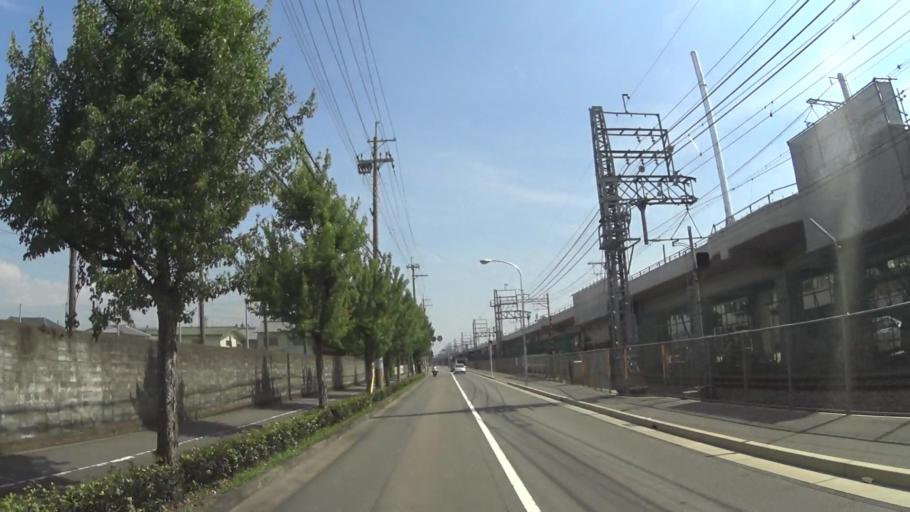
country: JP
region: Kyoto
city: Muko
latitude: 34.9720
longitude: 135.7032
